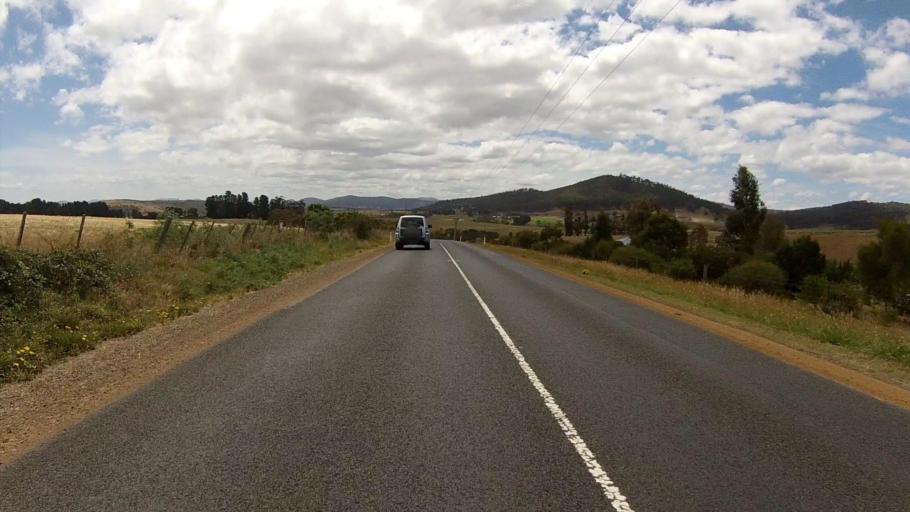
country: AU
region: Tasmania
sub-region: Sorell
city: Sorell
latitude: -42.8118
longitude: 147.6132
